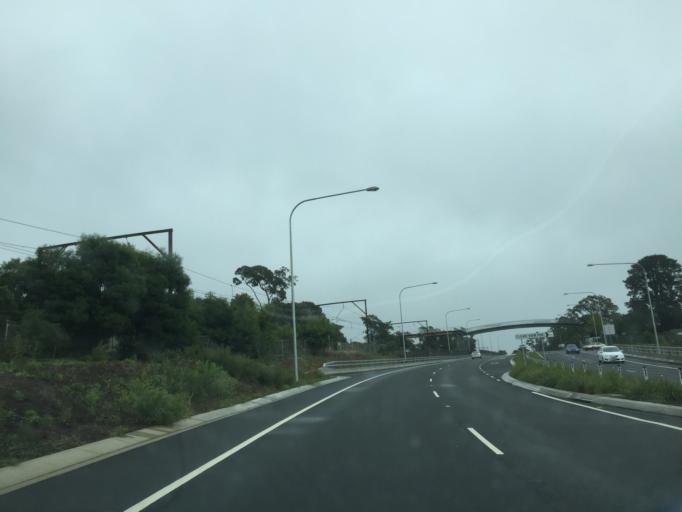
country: AU
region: New South Wales
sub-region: Blue Mountains Municipality
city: Hazelbrook
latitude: -33.7293
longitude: 150.4606
